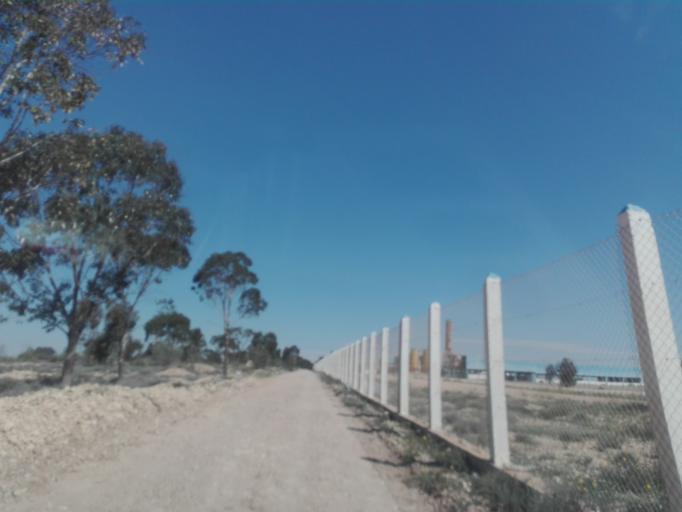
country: TN
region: Safaqis
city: Sfax
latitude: 34.7032
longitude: 10.5274
